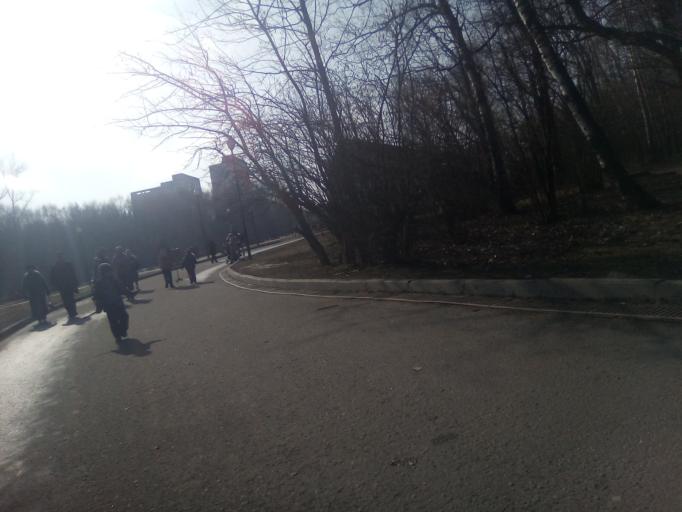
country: RU
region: Moscow
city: Tyoply Stan
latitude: 55.6367
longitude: 37.4916
